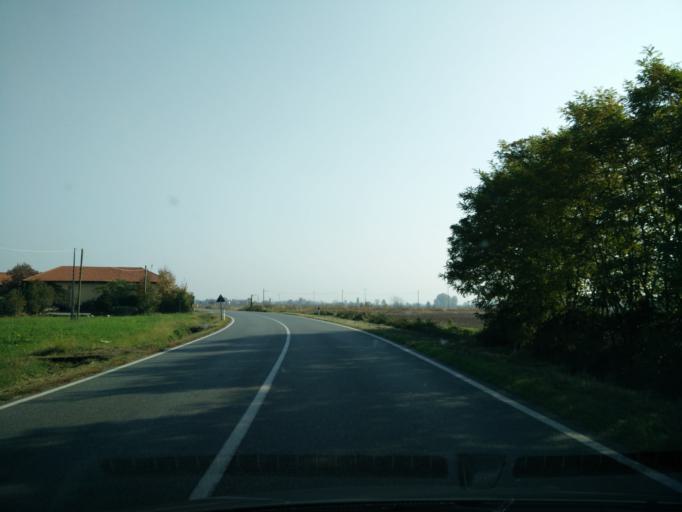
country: IT
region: Piedmont
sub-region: Provincia di Torino
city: Caselle Torinese
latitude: 45.1812
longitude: 7.6662
